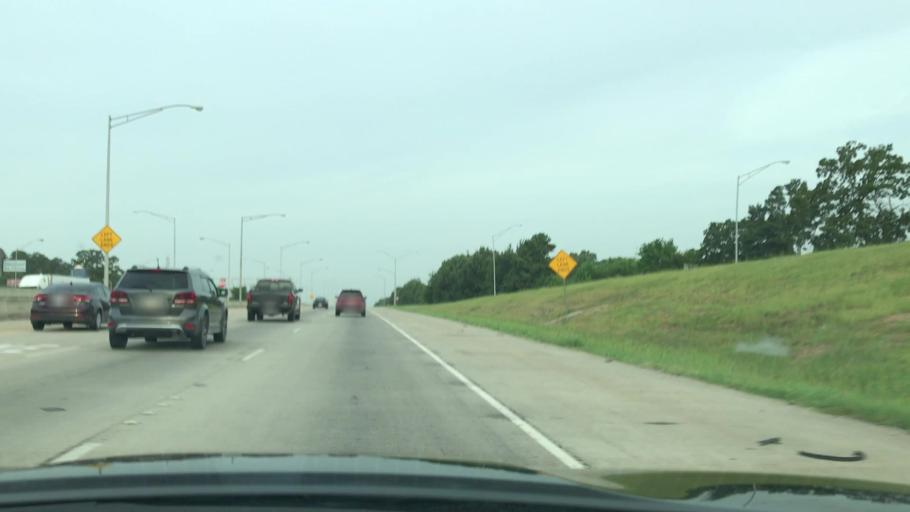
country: US
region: Louisiana
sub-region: Caddo Parish
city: Greenwood
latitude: 32.4506
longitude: -93.8673
